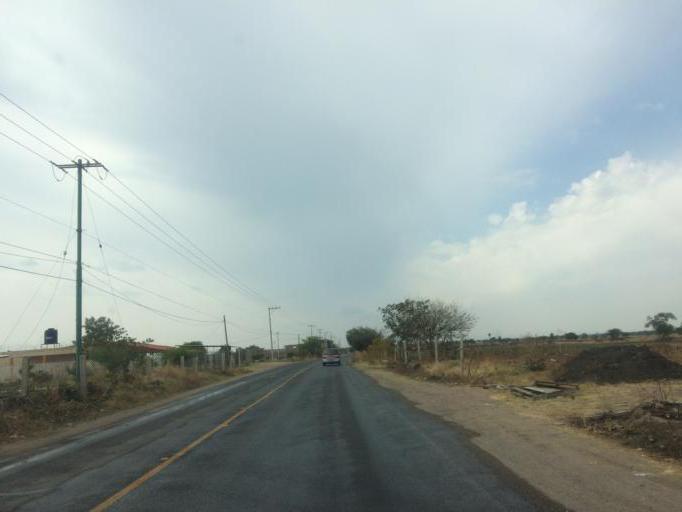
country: MX
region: Guanajuato
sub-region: Leon
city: Ladrilleras del Refugio
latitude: 21.0862
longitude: -101.5417
